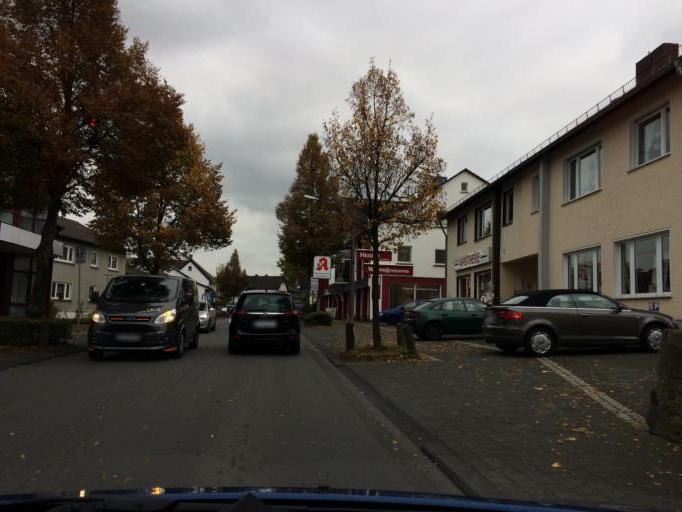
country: DE
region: North Rhine-Westphalia
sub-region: Regierungsbezirk Koln
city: Bad Honnef
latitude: 50.6798
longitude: 7.2653
